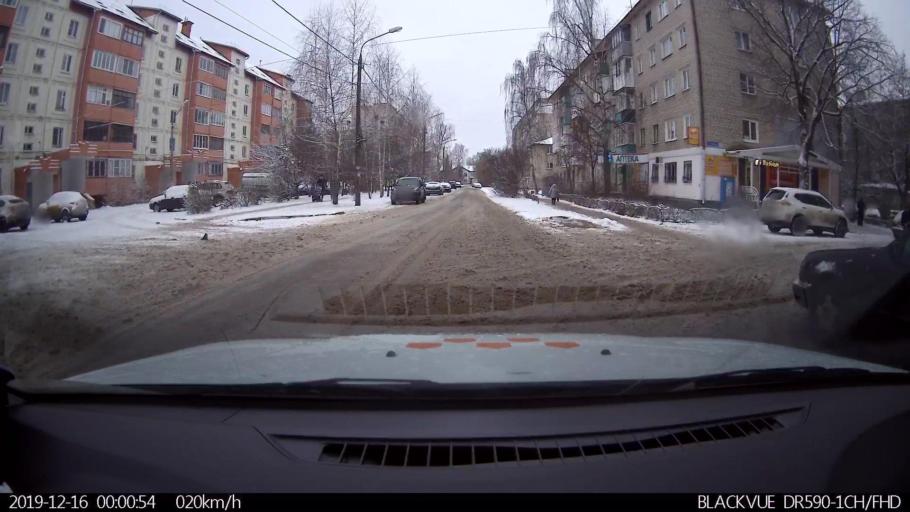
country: RU
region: Nizjnij Novgorod
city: Neklyudovo
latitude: 56.3596
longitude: 43.8481
